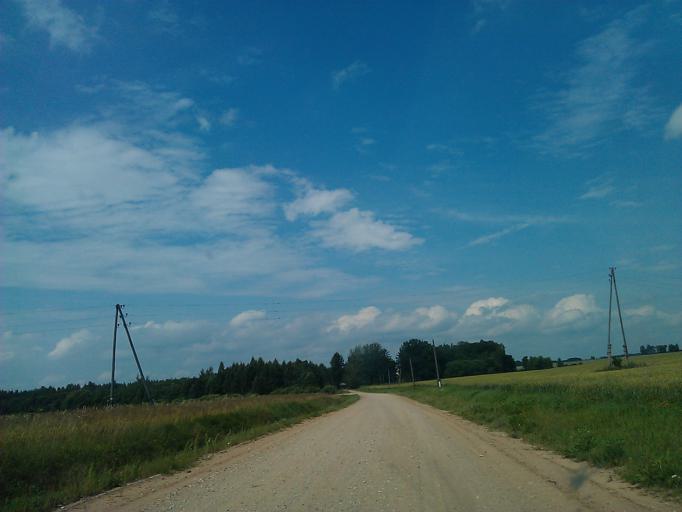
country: LV
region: Burtnieki
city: Matisi
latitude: 57.7085
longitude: 25.1540
